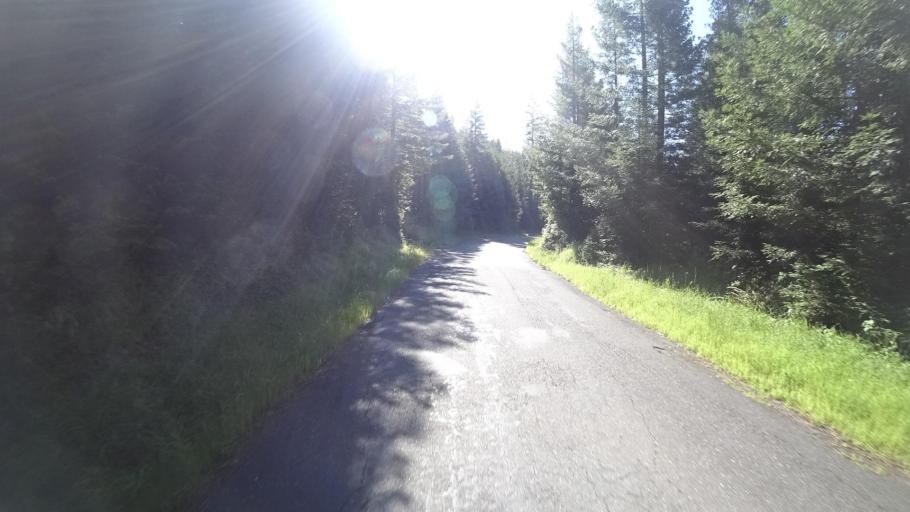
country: US
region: California
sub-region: Humboldt County
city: Rio Dell
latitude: 40.4561
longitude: -124.0329
